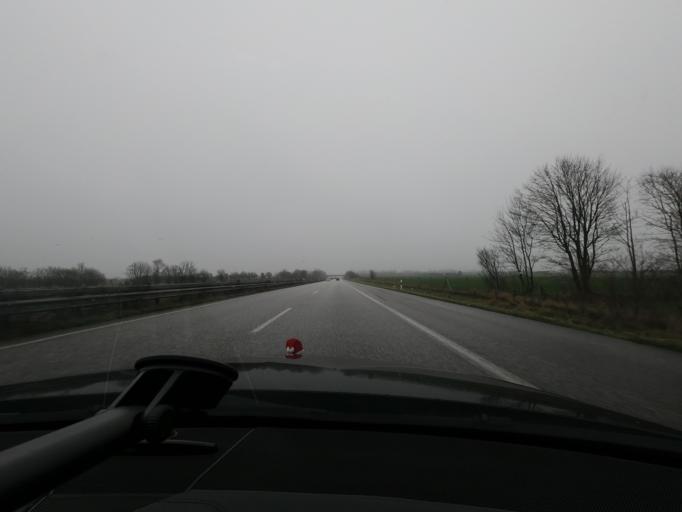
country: DE
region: Schleswig-Holstein
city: Tarp
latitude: 54.6443
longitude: 9.4371
